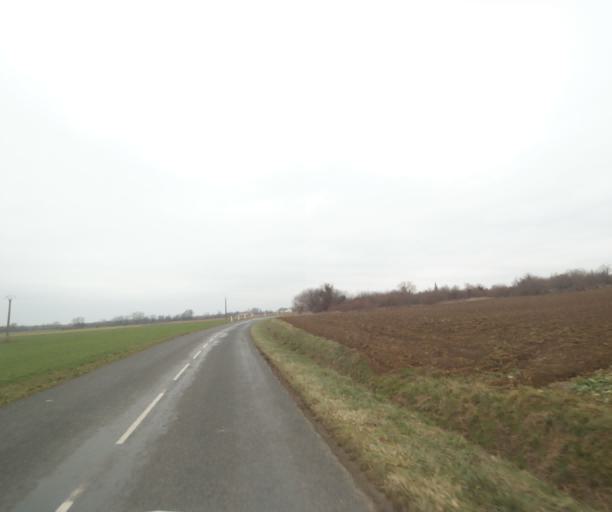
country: FR
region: Champagne-Ardenne
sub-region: Departement de la Haute-Marne
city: Villiers-en-Lieu
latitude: 48.6330
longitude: 4.7700
